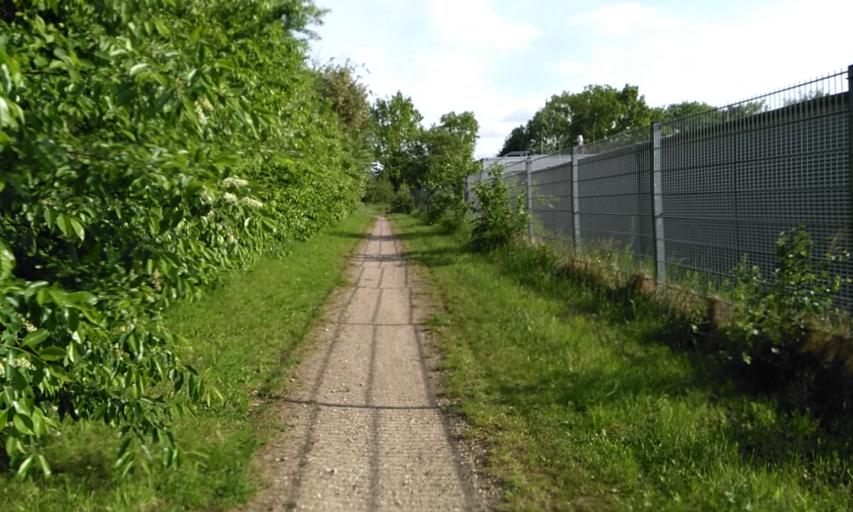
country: DE
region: Lower Saxony
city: Buxtehude
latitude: 53.4616
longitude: 9.7048
